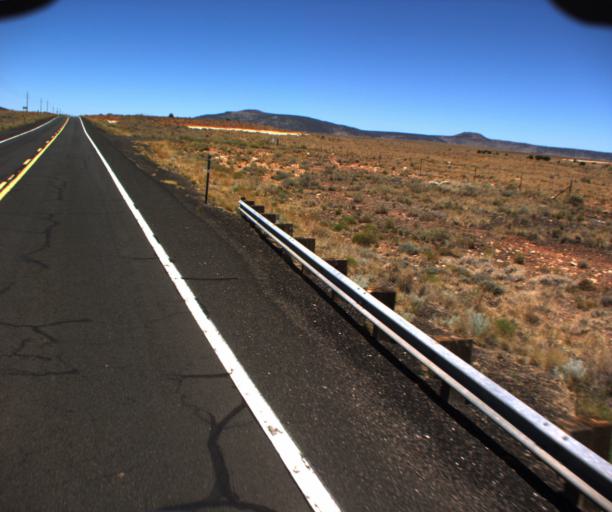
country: US
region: Arizona
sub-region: Coconino County
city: LeChee
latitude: 34.9065
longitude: -110.8434
